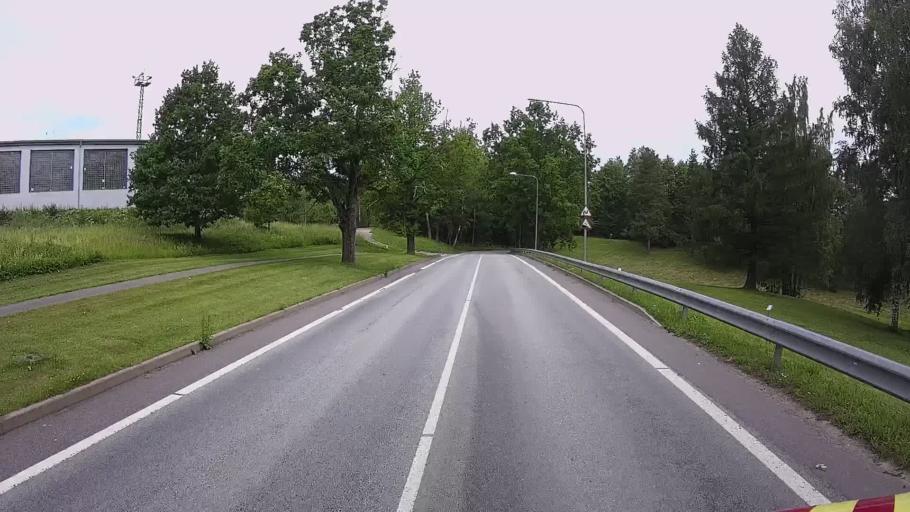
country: EE
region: Viljandimaa
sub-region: Karksi vald
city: Karksi-Nuia
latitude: 58.1066
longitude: 25.5469
